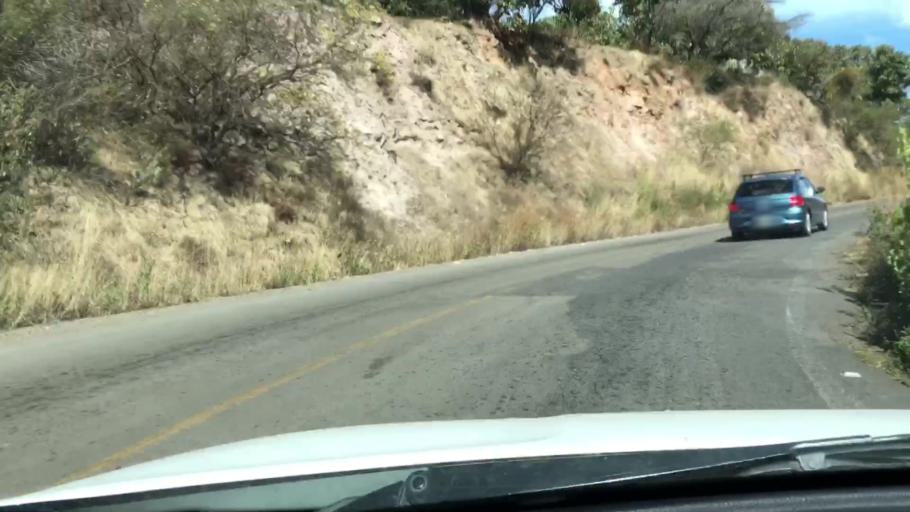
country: MX
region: Jalisco
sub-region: Zacoalco de Torres
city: Barranca de Otates (Barranca de Otatan)
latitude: 20.1937
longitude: -103.6946
